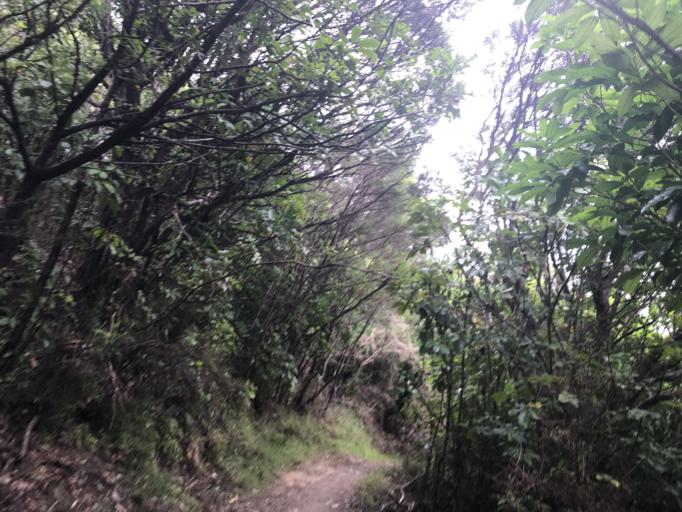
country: NZ
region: Marlborough
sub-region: Marlborough District
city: Picton
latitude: -41.2145
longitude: 173.9874
